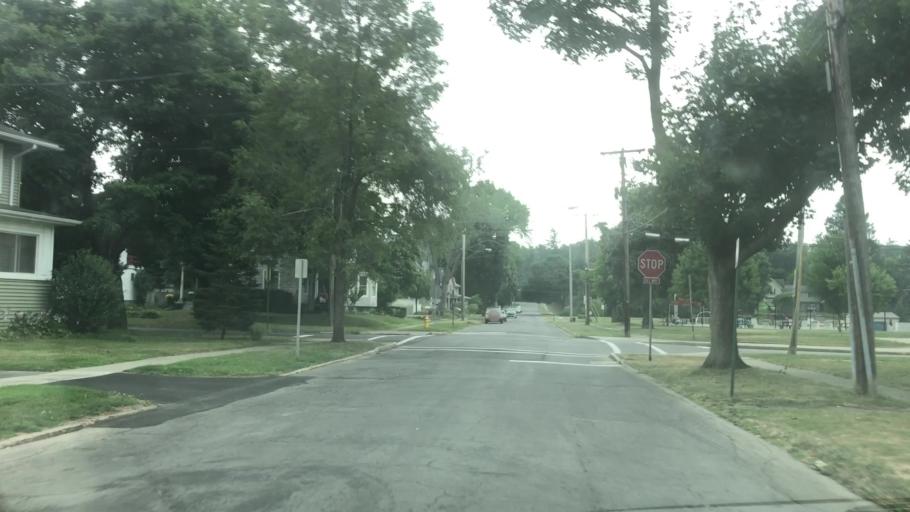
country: US
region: New York
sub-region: Monroe County
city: East Rochester
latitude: 43.1109
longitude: -77.4827
